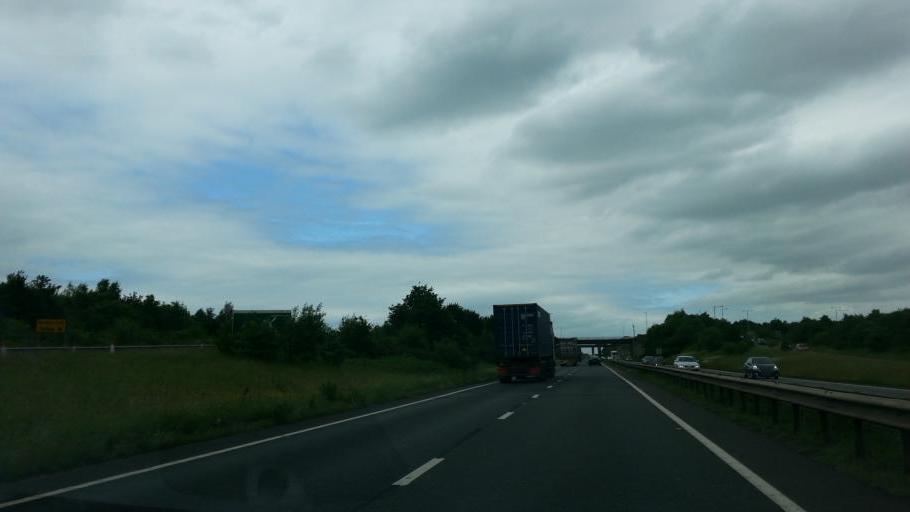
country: GB
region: England
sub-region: Leicestershire
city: Ashby de la Zouch
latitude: 52.7467
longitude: -1.4504
